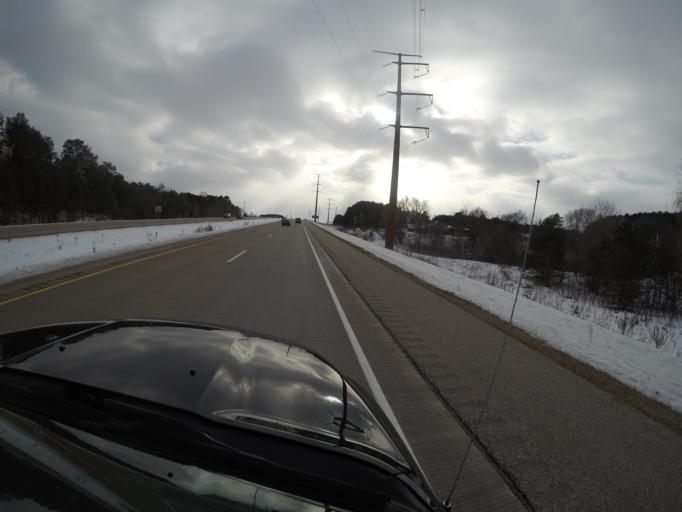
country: US
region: Wisconsin
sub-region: La Crosse County
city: Holmen
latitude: 43.9734
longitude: -91.2863
